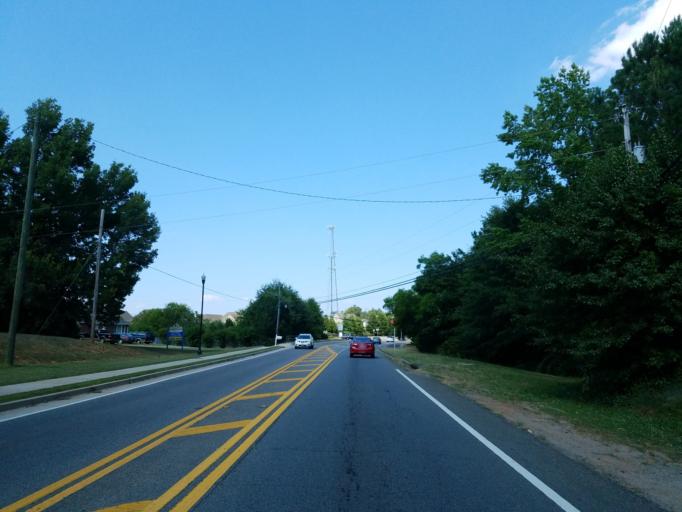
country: US
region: Georgia
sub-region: Fulton County
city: Alpharetta
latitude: 34.0880
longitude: -84.3508
